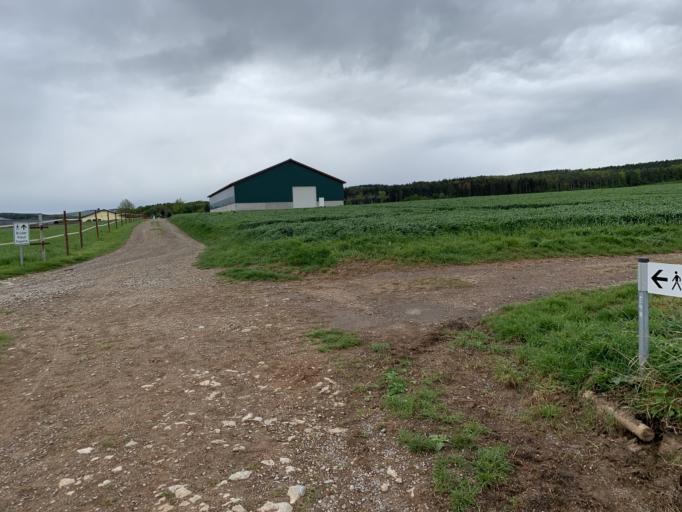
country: DE
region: North Rhine-Westphalia
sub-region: Regierungsbezirk Koln
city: Bad Munstereifel
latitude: 50.5957
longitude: 6.7326
